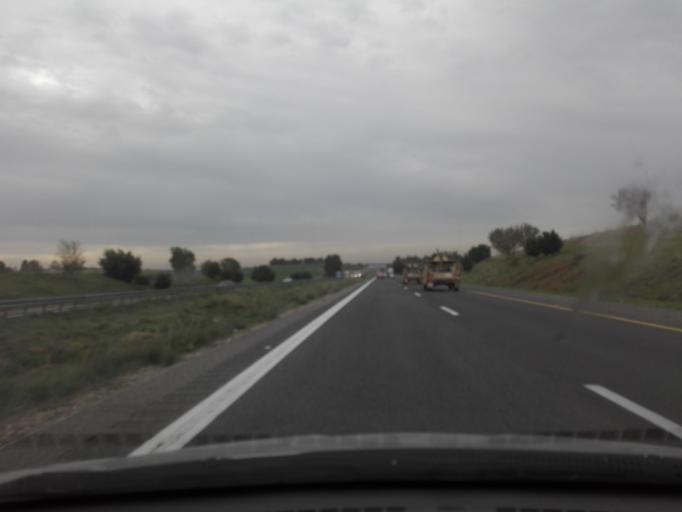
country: IL
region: Central District
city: Mazkeret Batya
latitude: 31.8470
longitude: 34.8665
